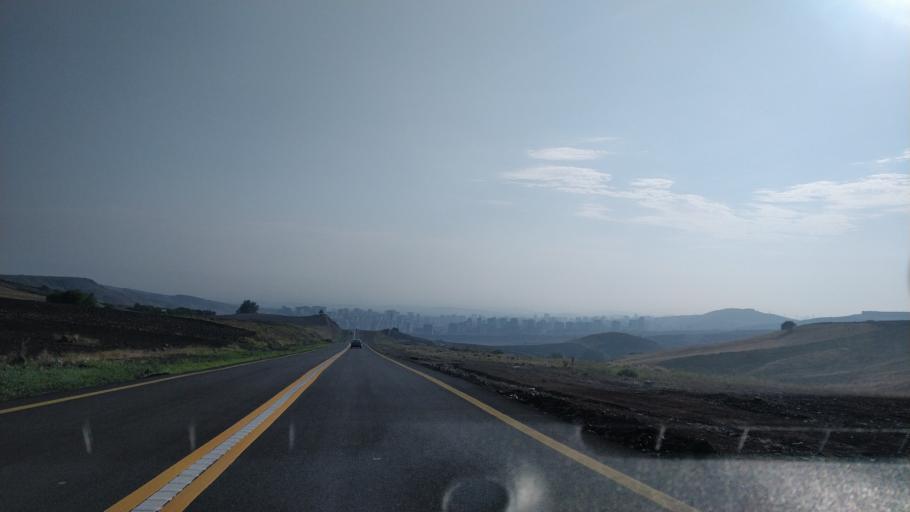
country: TR
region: Ankara
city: Etimesgut
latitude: 39.8711
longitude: 32.5922
